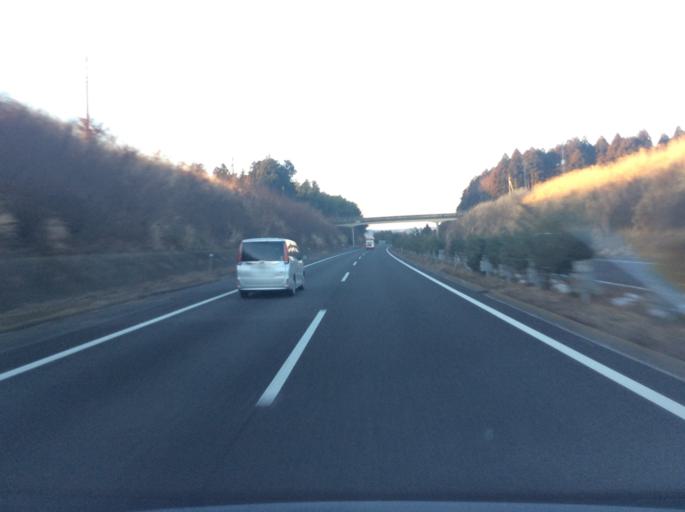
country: JP
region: Ibaraki
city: Hitachi-Naka
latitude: 36.4346
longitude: 140.4501
